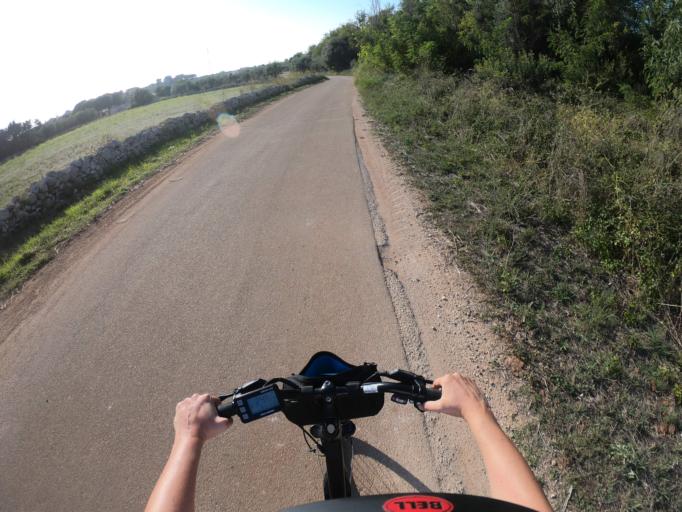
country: IT
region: Apulia
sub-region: Provincia di Lecce
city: Leuca
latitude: 39.8166
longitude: 18.3600
